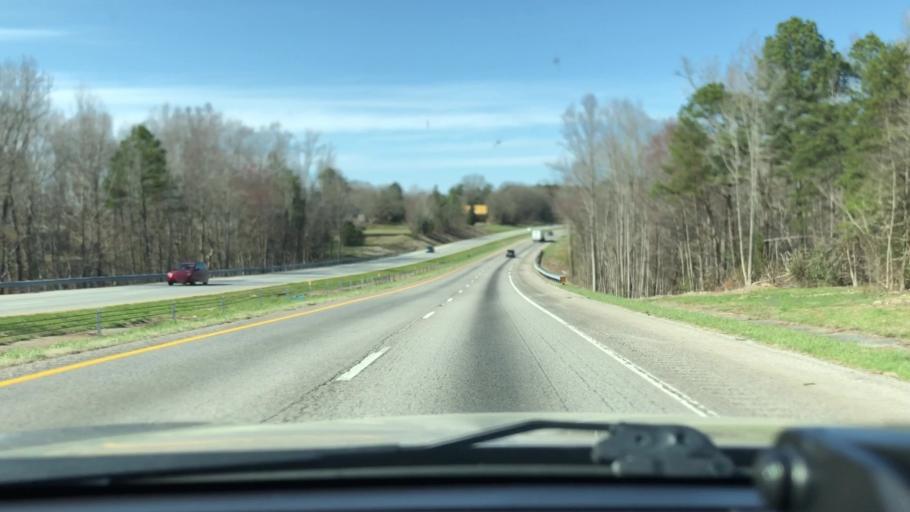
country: US
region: South Carolina
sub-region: Spartanburg County
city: Roebuck
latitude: 34.8831
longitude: -81.9925
